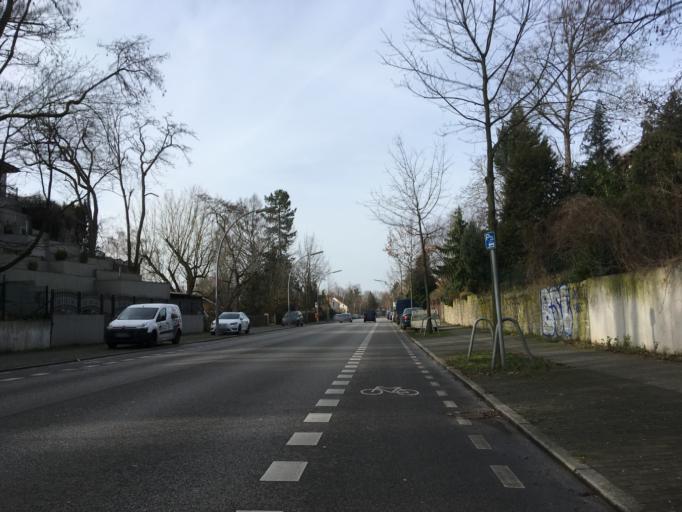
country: DE
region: Berlin
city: Lubars
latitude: 52.6144
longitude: 13.3566
